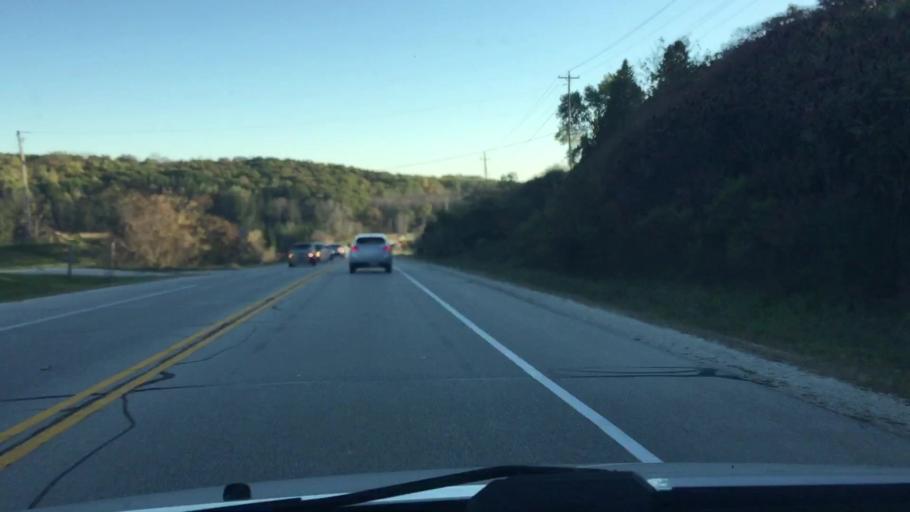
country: US
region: Wisconsin
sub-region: Waukesha County
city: Wales
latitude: 43.0367
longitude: -88.3741
